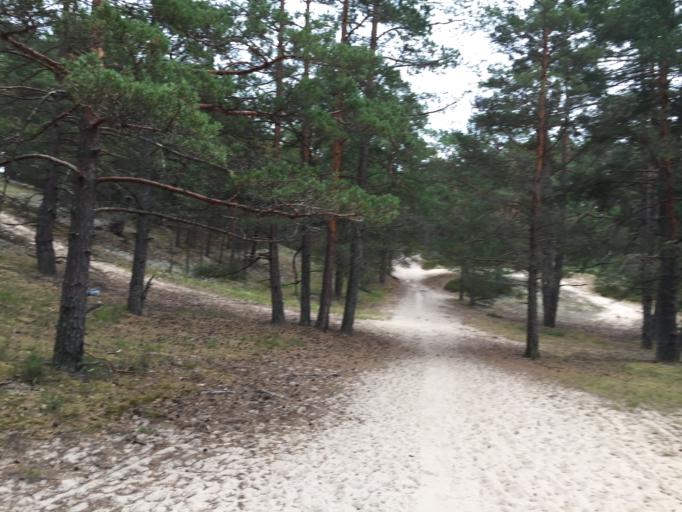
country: LV
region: Carnikava
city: Carnikava
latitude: 57.1227
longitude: 24.2157
